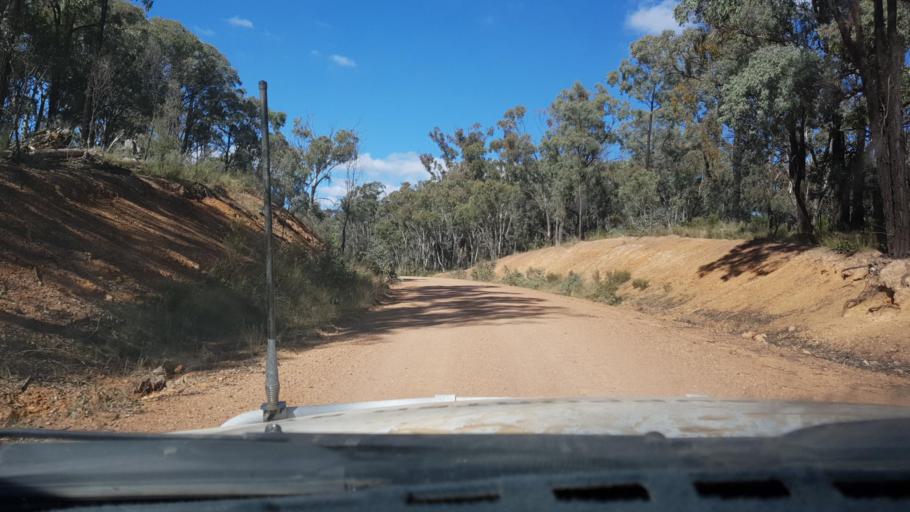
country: AU
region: New South Wales
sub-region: Tamworth Municipality
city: Manilla
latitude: -30.4537
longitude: 150.8776
